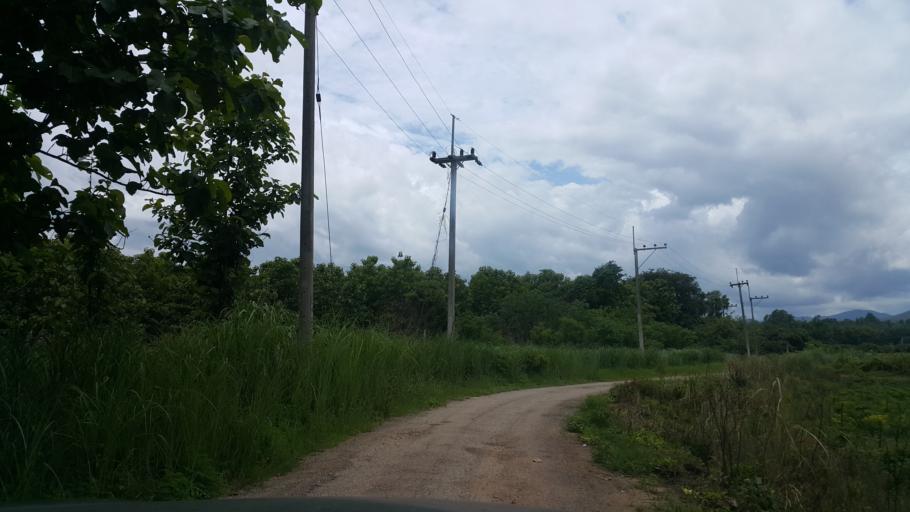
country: TH
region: Chiang Mai
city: Mae Taeng
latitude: 19.1948
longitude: 98.9858
